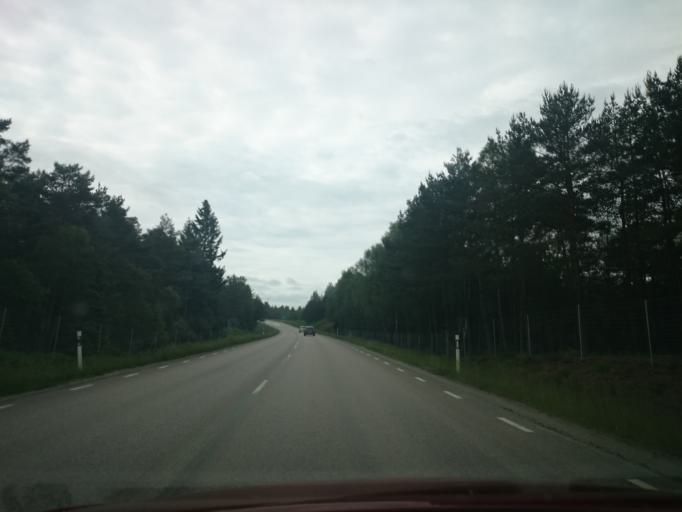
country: SE
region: Vaestra Goetaland
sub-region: Harryda Kommun
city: Hindas
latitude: 57.6788
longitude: 12.3563
